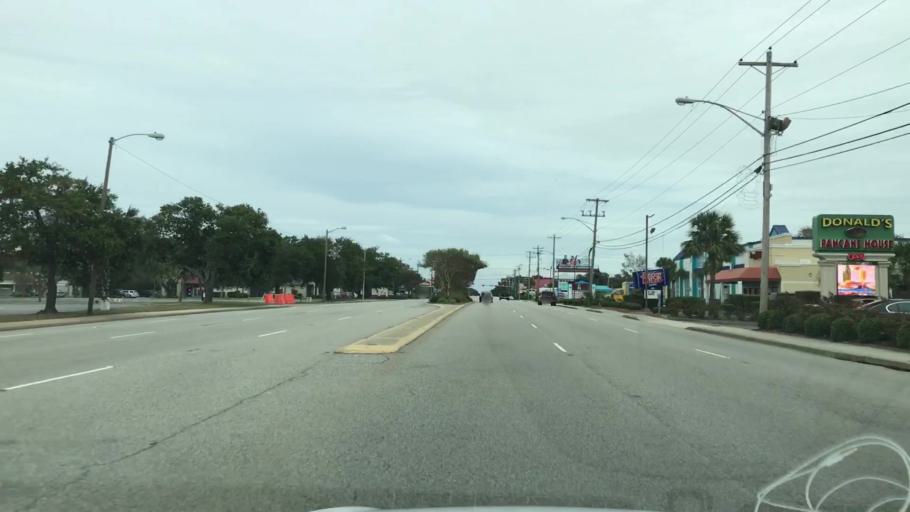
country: US
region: South Carolina
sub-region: Horry County
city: Myrtle Beach
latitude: 33.7066
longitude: -78.8669
